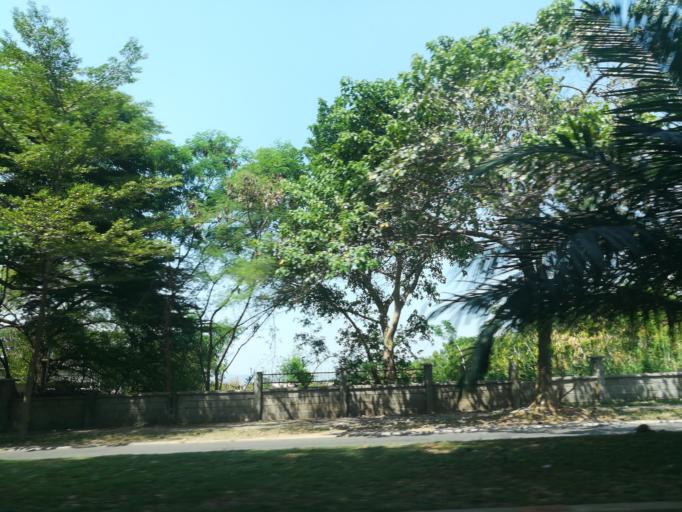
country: NG
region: Abuja Federal Capital Territory
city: Abuja
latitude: 9.0720
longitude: 7.4278
